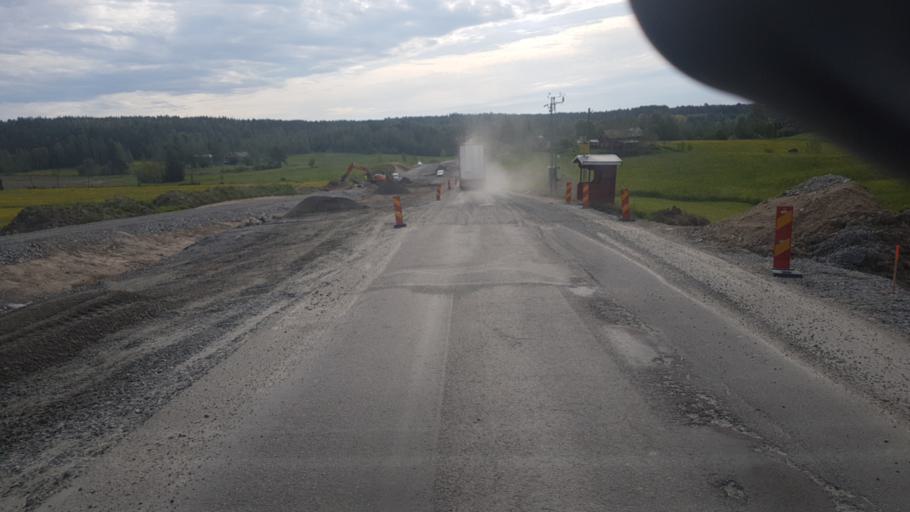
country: SE
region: Vaermland
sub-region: Arvika Kommun
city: Arvika
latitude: 59.7096
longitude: 12.5513
